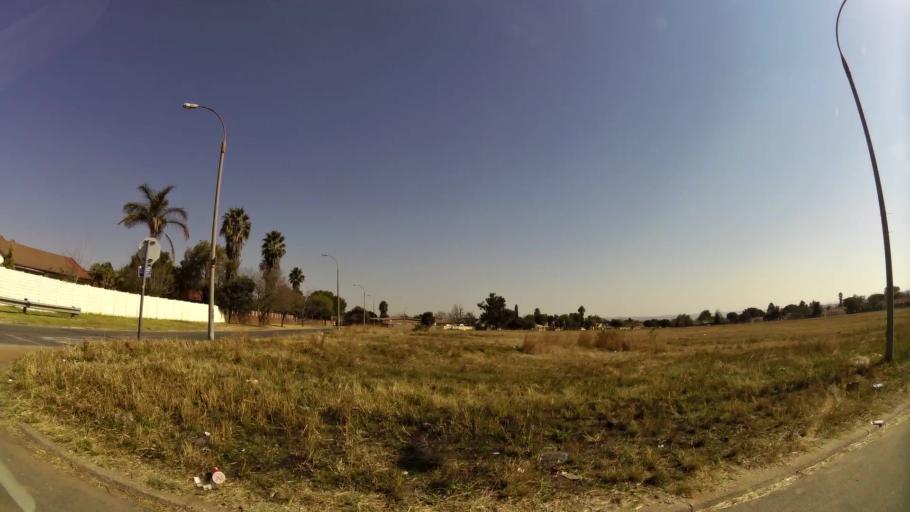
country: ZA
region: Gauteng
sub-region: Ekurhuleni Metropolitan Municipality
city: Tembisa
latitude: -26.0485
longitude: 28.2301
